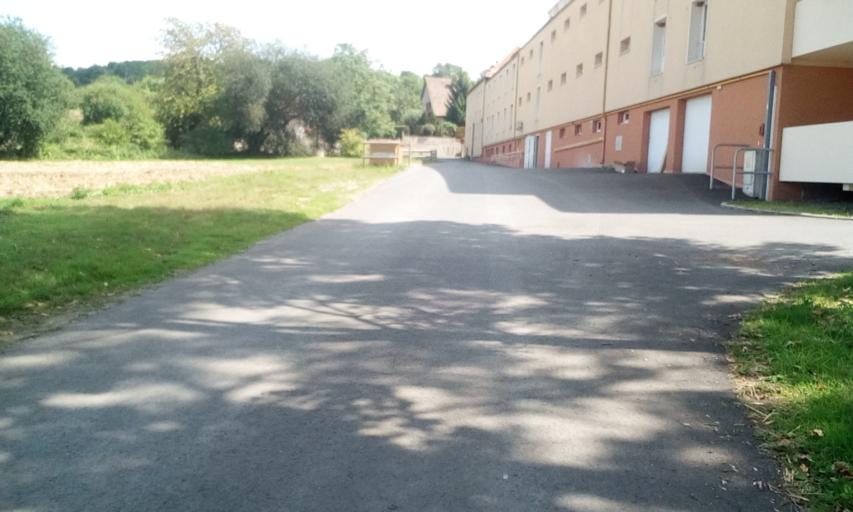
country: FR
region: Lower Normandy
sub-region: Departement du Calvados
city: Argences
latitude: 49.1420
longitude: -0.1649
